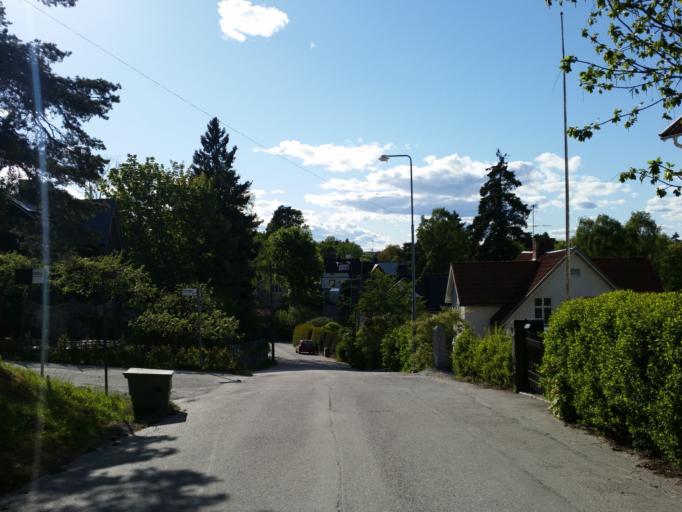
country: SE
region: Stockholm
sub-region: Sundbybergs Kommun
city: Sundbyberg
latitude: 59.3735
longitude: 17.9581
